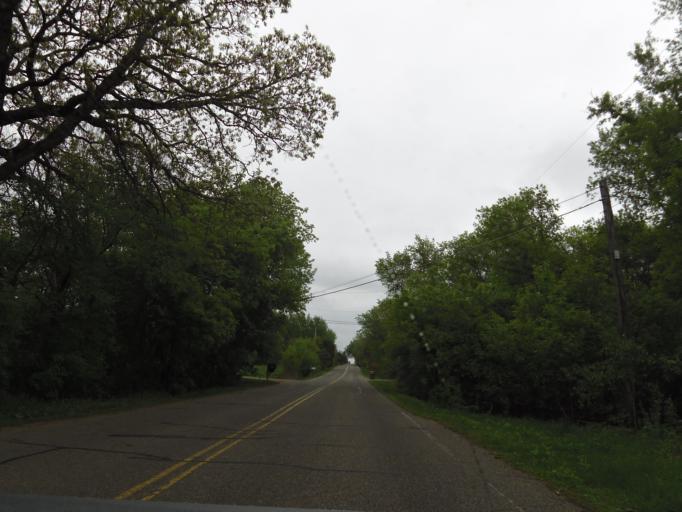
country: US
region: Minnesota
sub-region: Washington County
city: Oak Park Heights
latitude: 44.9925
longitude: -92.8265
